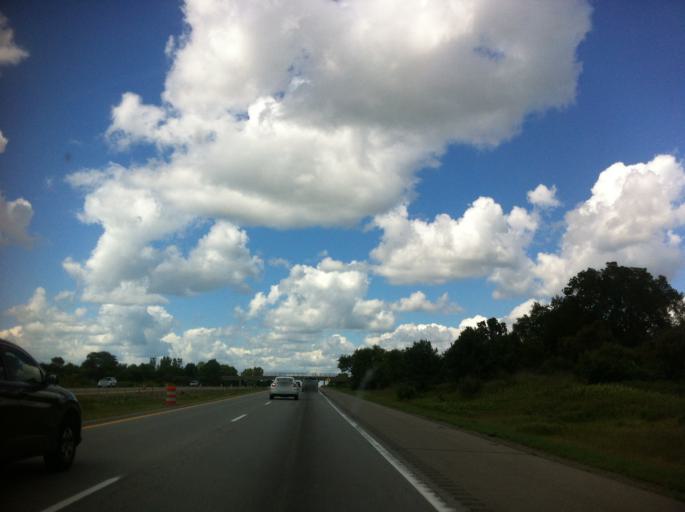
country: US
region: Michigan
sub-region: Washtenaw County
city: Milan
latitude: 42.1533
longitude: -83.6837
